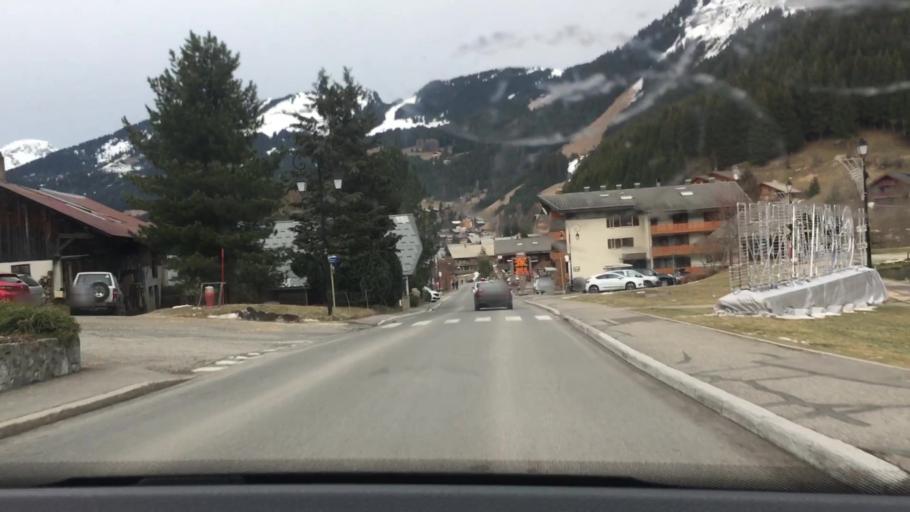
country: FR
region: Rhone-Alpes
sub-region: Departement de la Haute-Savoie
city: Chatel
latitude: 46.2571
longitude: 6.8402
